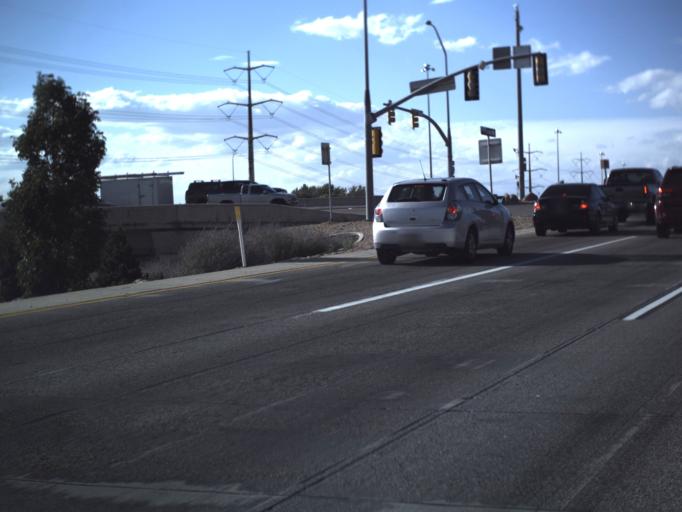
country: US
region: Utah
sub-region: Utah County
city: Provo
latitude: 40.2077
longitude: -111.6582
